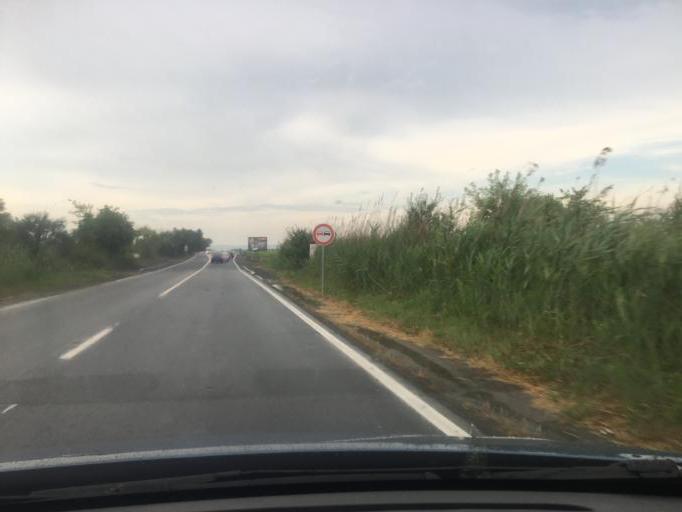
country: BG
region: Burgas
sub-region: Obshtina Pomorie
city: Pomorie
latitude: 42.5933
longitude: 27.6137
